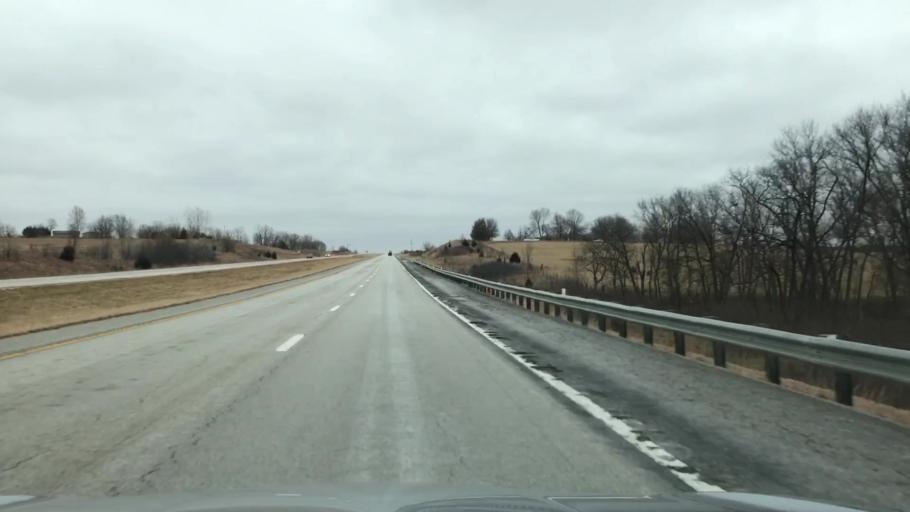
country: US
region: Missouri
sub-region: Caldwell County
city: Hamilton
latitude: 39.7498
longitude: -94.0979
